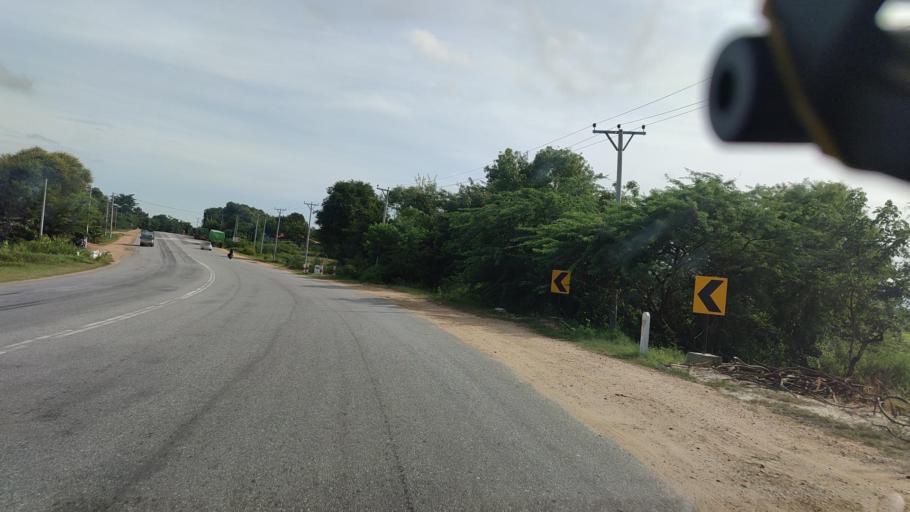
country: MM
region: Mandalay
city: Yamethin
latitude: 20.3356
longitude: 96.1608
